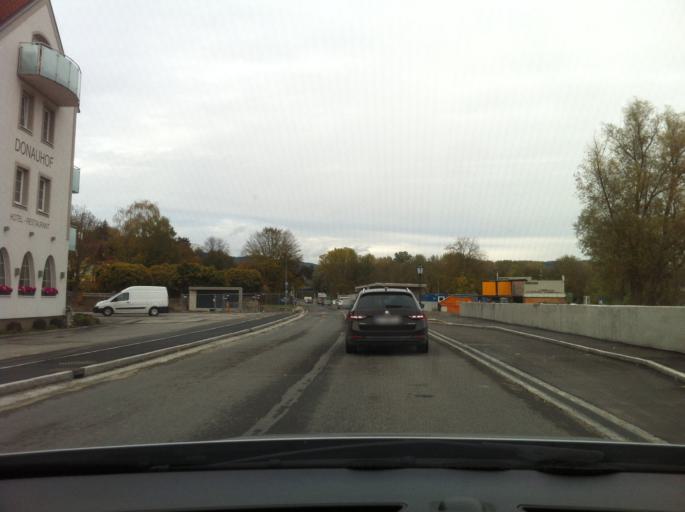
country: AT
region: Lower Austria
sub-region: Politischer Bezirk Melk
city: Emmersdorf an der Donau
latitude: 48.2414
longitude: 15.3381
